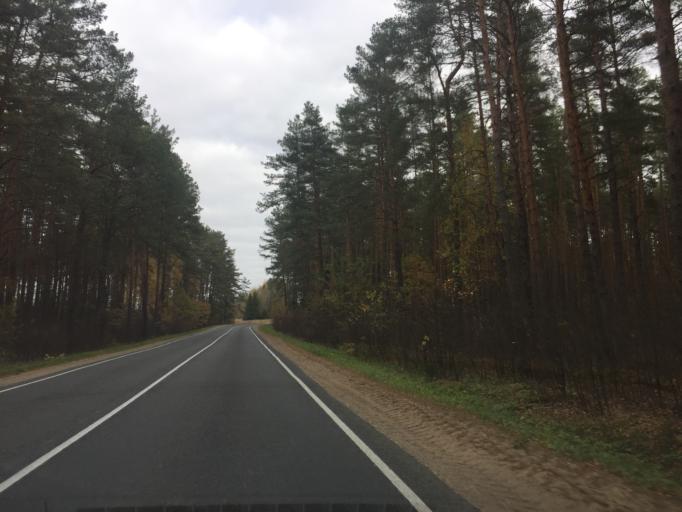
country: BY
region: Minsk
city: Svir
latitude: 54.8211
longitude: 26.1828
